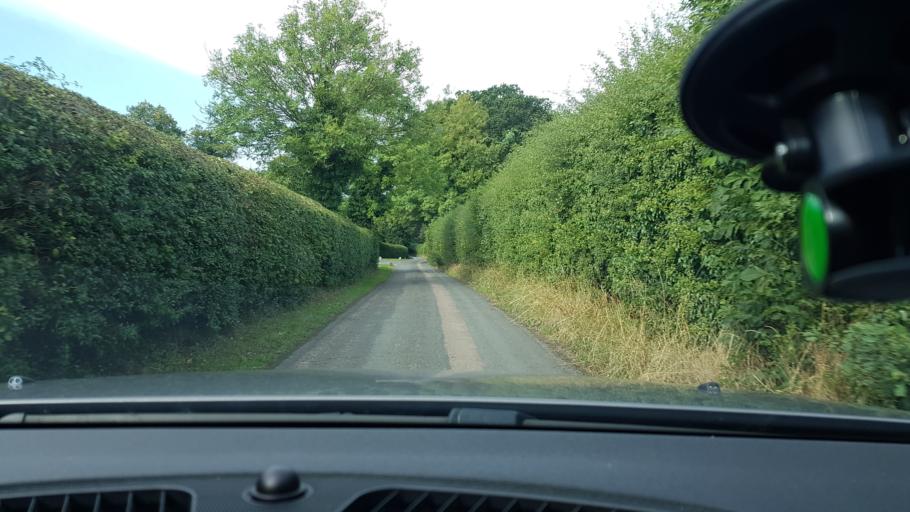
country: GB
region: England
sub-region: West Berkshire
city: Hungerford
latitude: 51.4245
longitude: -1.4821
